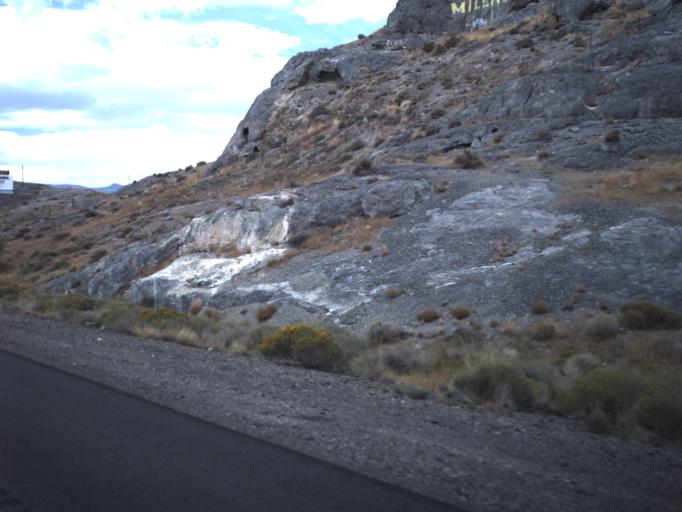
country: US
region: Utah
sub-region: Tooele County
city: Wendover
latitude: 40.7398
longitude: -114.0363
